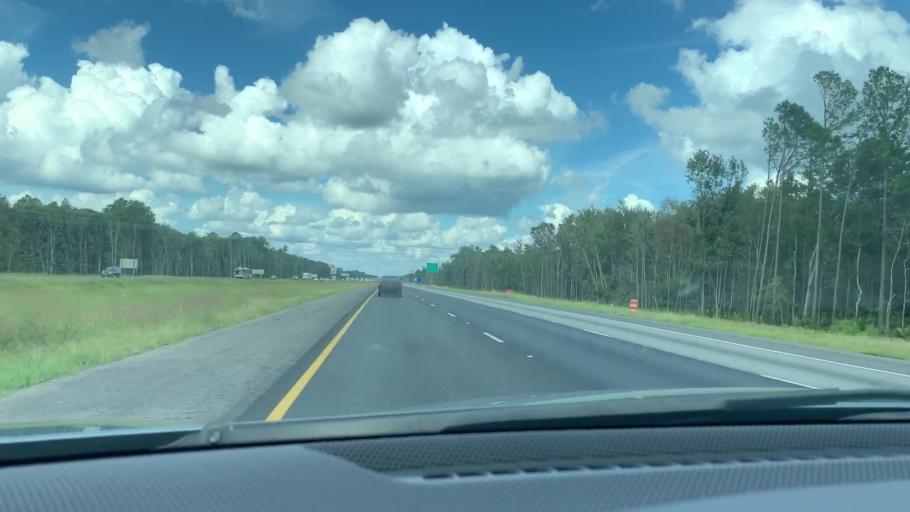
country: US
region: Georgia
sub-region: Camden County
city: Kingsland
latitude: 30.8039
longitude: -81.6615
